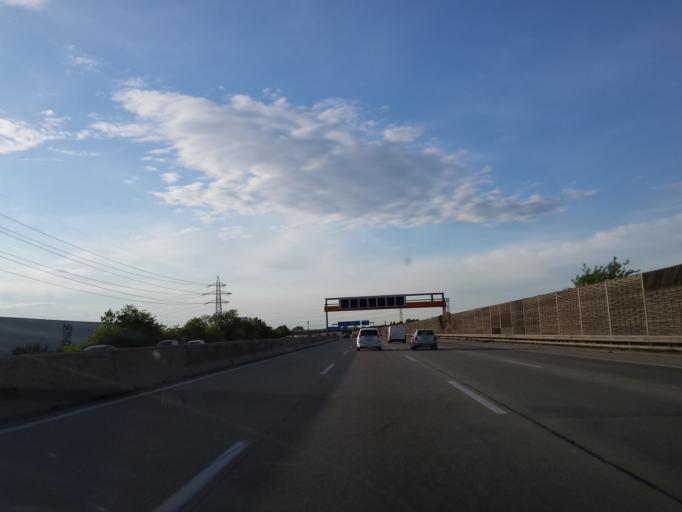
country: AT
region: Lower Austria
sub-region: Politischer Bezirk Modling
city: Biedermannsdorf
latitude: 48.0732
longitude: 16.3379
